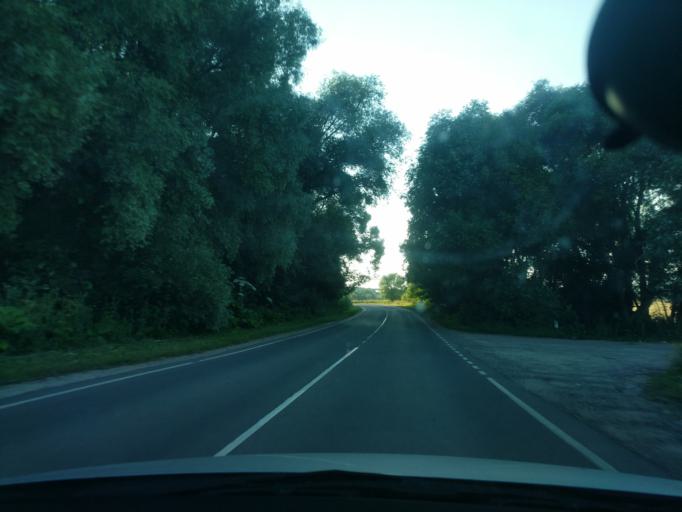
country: RU
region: Moskovskaya
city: Serpukhov
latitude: 54.8519
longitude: 37.4893
